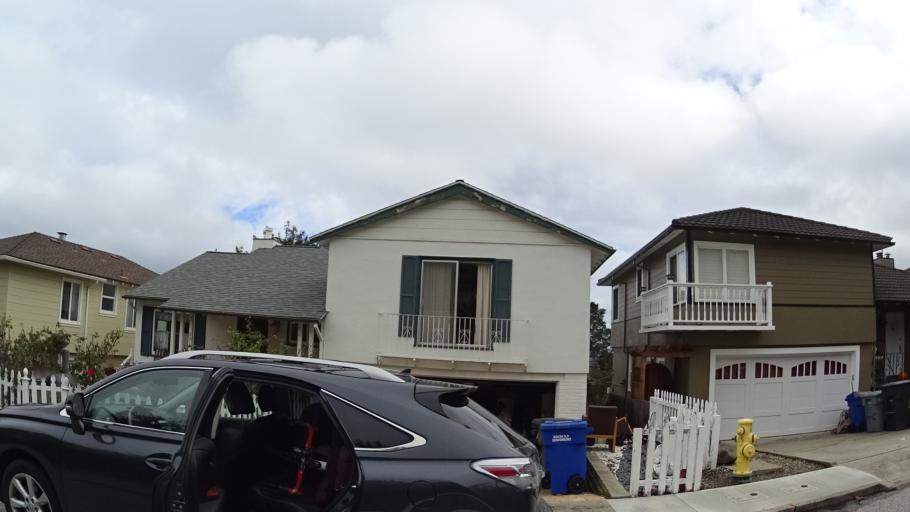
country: US
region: California
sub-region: San Mateo County
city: Millbrae
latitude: 37.5952
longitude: -122.4056
